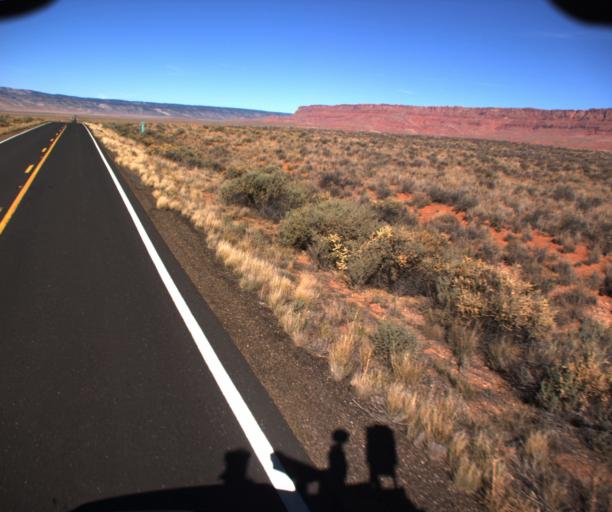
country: US
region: Arizona
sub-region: Coconino County
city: Page
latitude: 36.6933
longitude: -111.8970
